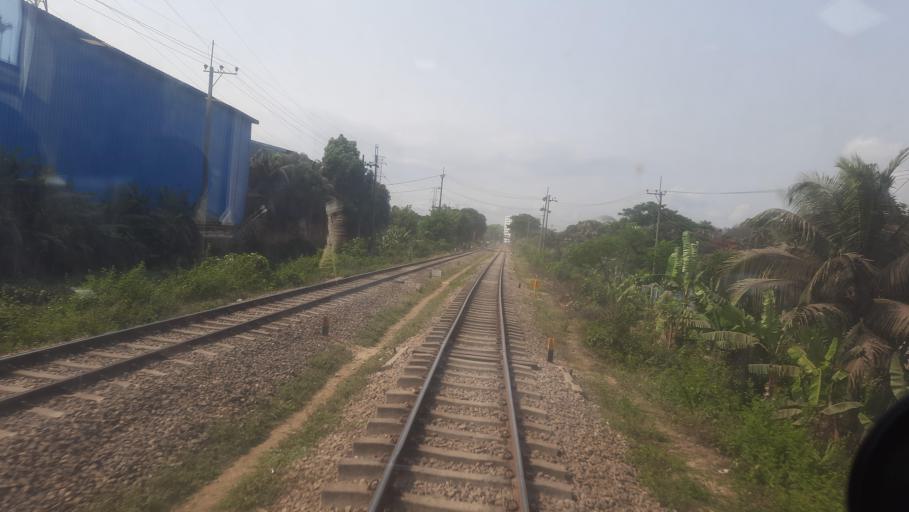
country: BD
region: Chittagong
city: Chittagong
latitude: 22.4143
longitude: 91.7546
